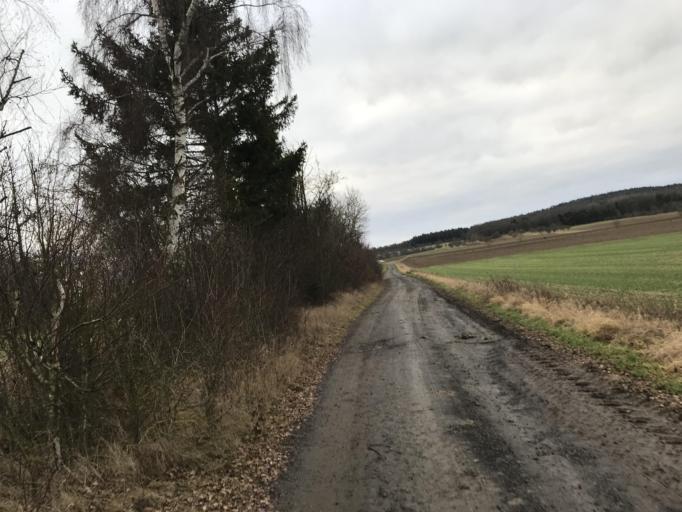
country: DE
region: Hesse
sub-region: Regierungsbezirk Darmstadt
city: Butzbach
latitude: 50.4611
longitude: 8.6392
